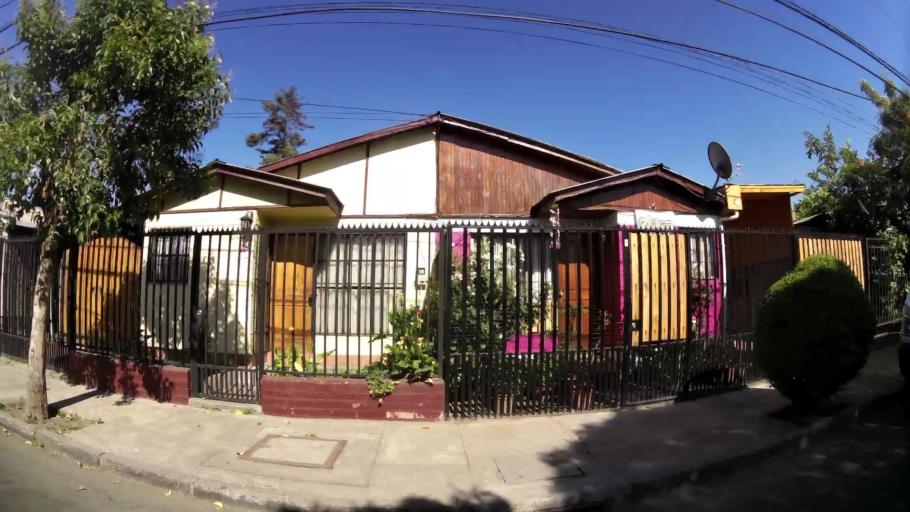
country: CL
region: Santiago Metropolitan
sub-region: Provincia de Maipo
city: San Bernardo
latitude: -33.5718
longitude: -70.7053
